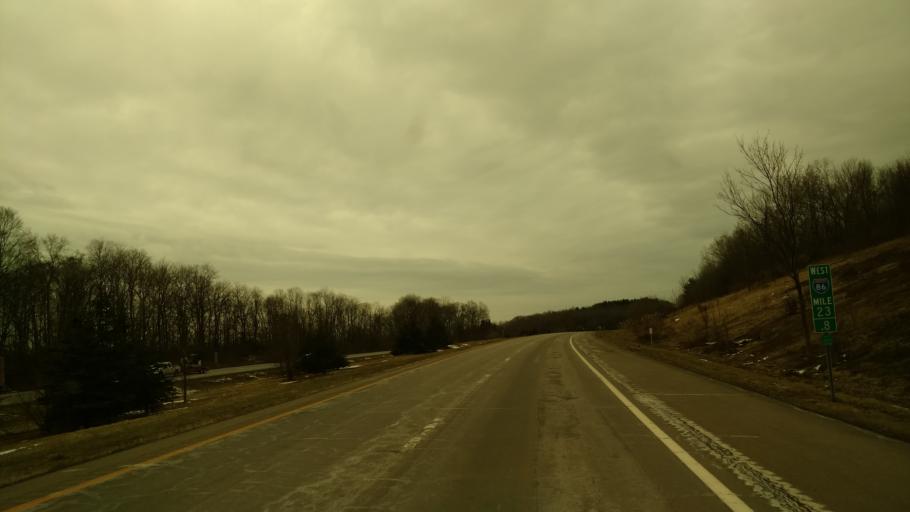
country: US
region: New York
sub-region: Chautauqua County
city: Lakewood
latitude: 42.1291
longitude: -79.3199
